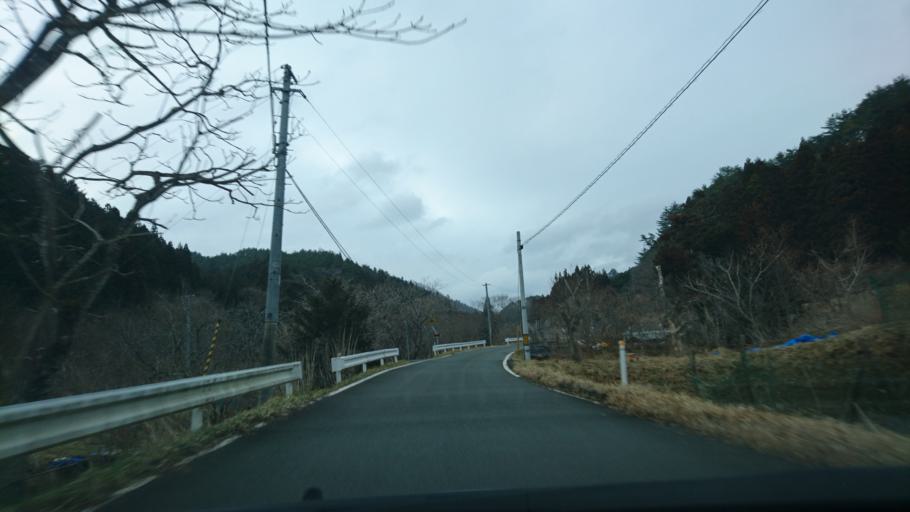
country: JP
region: Iwate
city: Ofunato
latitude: 38.9857
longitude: 141.5535
